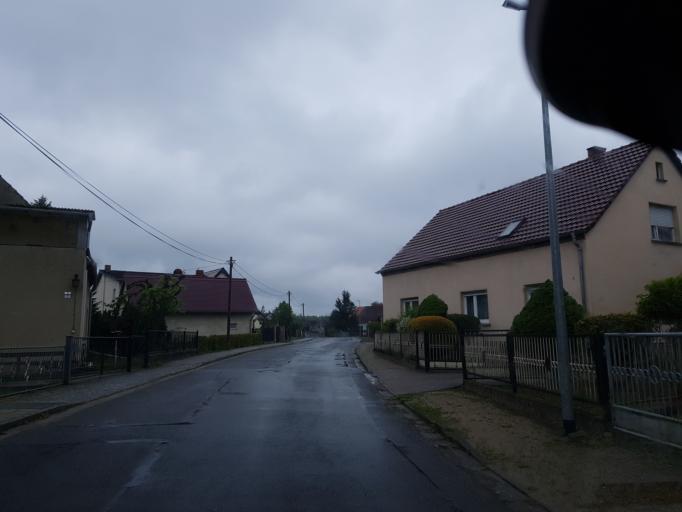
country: DE
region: Brandenburg
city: Tschernitz
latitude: 51.6373
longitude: 14.5996
